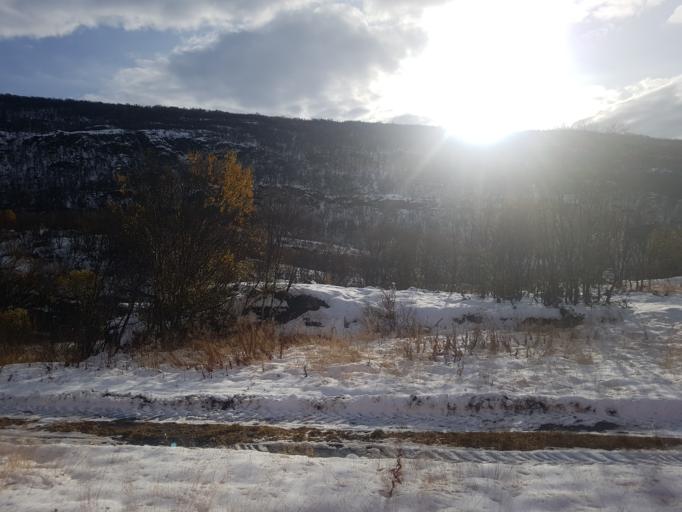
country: NO
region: Sor-Trondelag
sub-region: Oppdal
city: Oppdal
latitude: 62.3062
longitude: 9.6065
